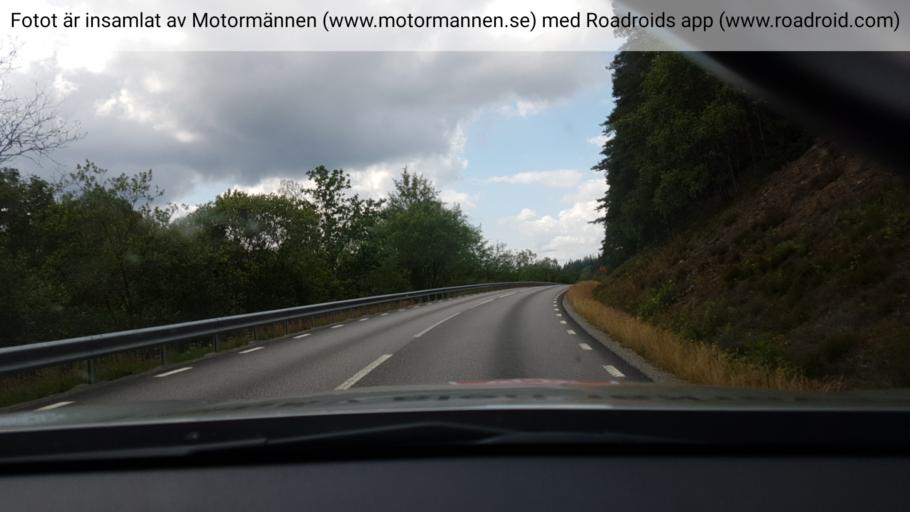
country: SE
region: Vaestra Goetaland
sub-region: Svenljunga Kommun
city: Svenljunga
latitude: 57.4680
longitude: 13.2266
